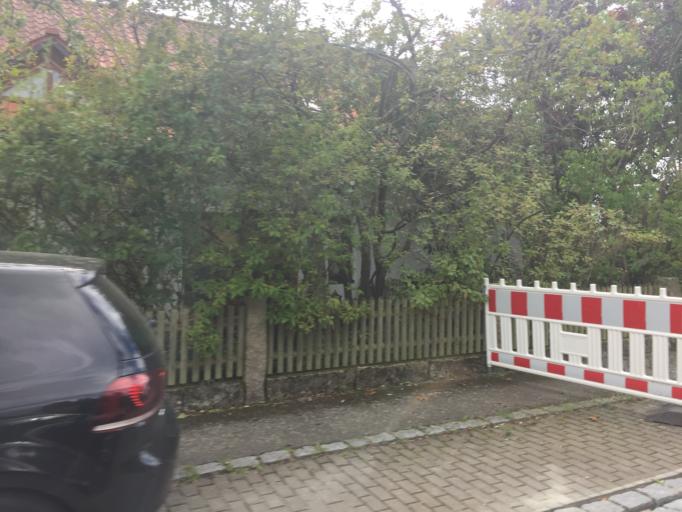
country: DE
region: Bavaria
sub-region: Upper Palatinate
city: Pressath
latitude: 49.7717
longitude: 11.9438
